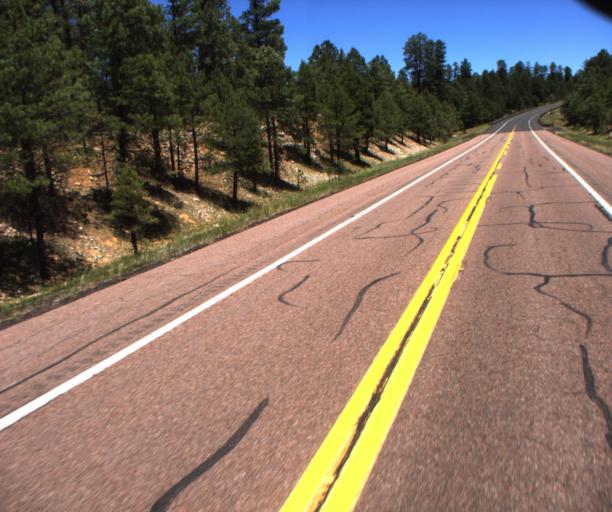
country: US
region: Arizona
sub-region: Gila County
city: Pine
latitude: 34.5504
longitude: -111.3132
